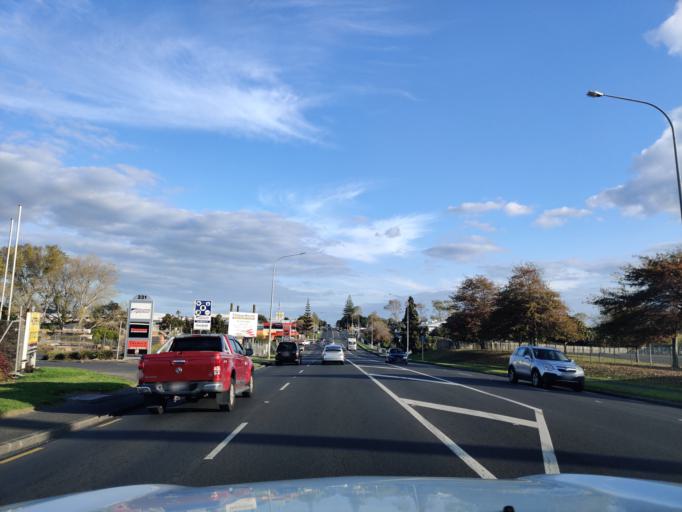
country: NZ
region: Auckland
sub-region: Auckland
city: Manukau City
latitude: -36.9545
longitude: 174.8907
